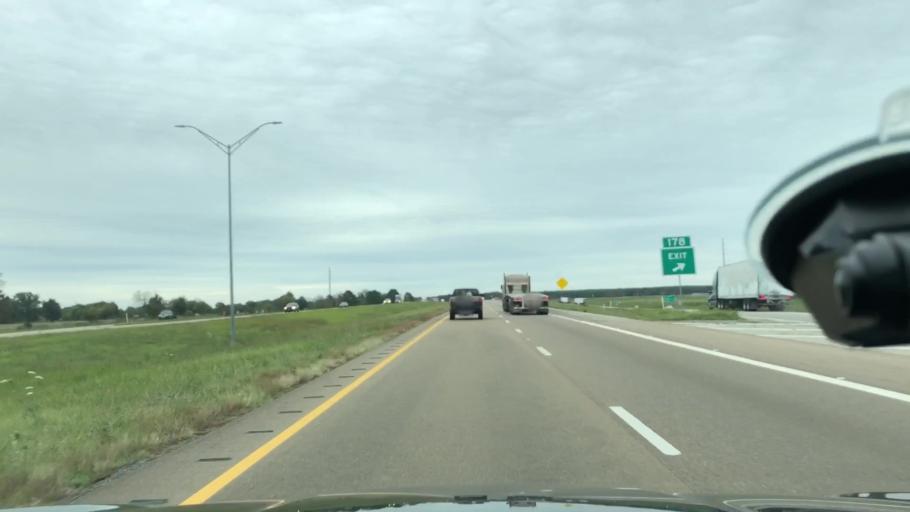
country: US
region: Texas
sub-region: Morris County
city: Naples
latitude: 33.2938
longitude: -94.7424
